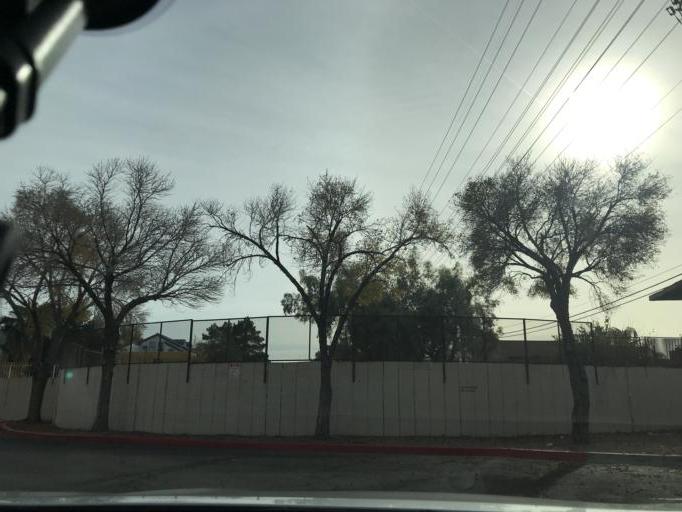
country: US
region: Nevada
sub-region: Clark County
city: Las Vegas
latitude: 36.1737
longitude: -115.1647
